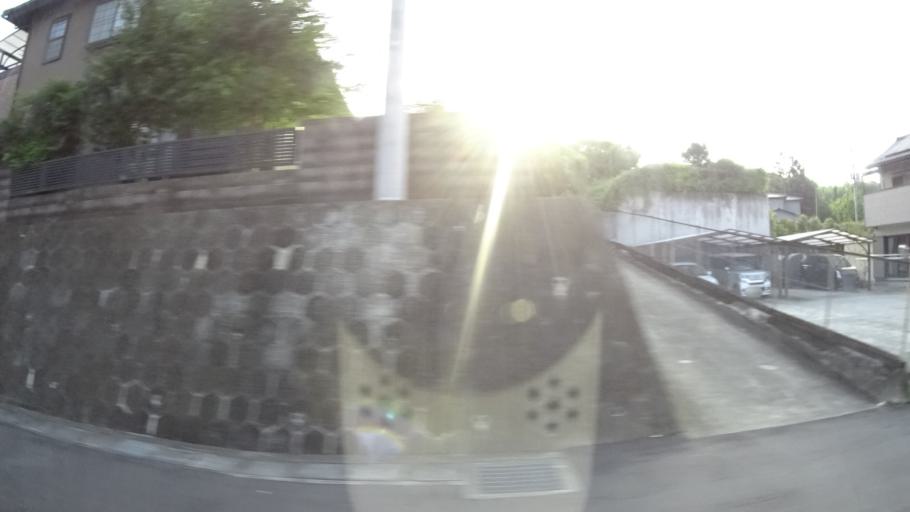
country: JP
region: Tochigi
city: Karasuyama
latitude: 36.6409
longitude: 140.1533
